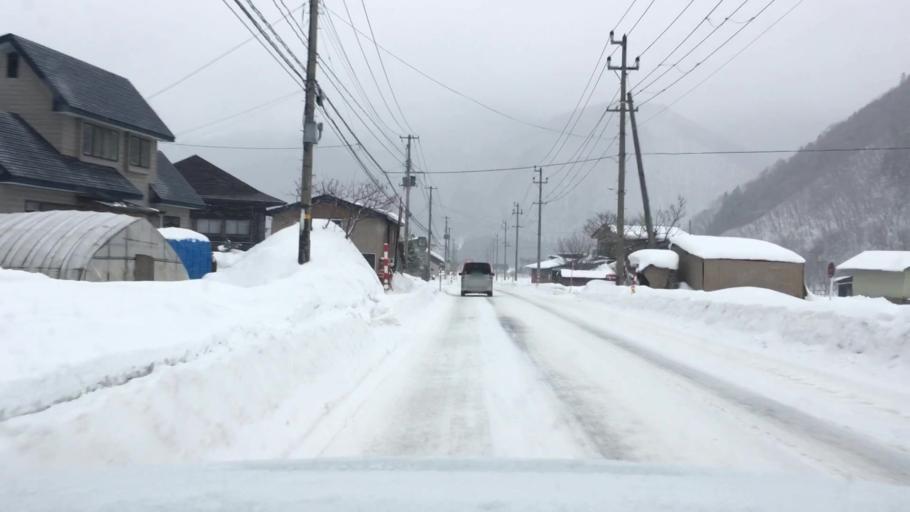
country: JP
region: Akita
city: Hanawa
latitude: 40.0754
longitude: 141.0208
